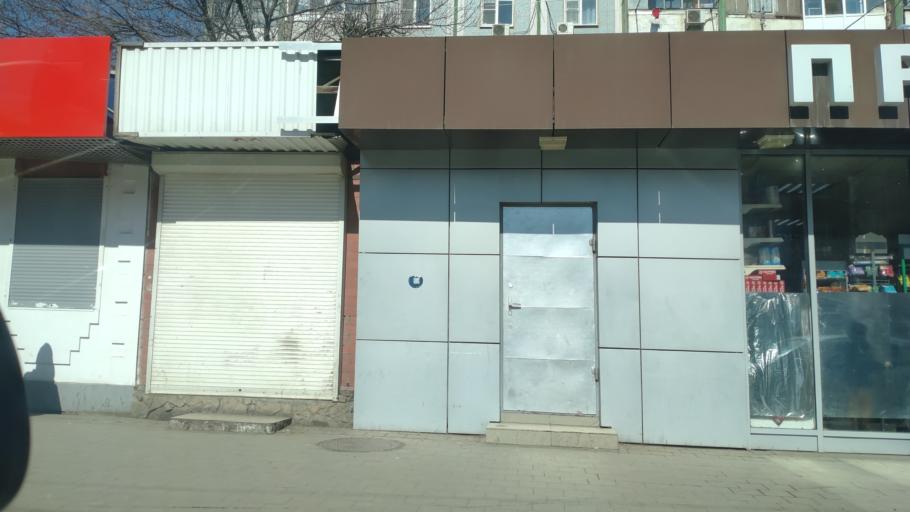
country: RU
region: Krasnodarskiy
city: Krasnodar
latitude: 45.0558
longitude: 39.0216
